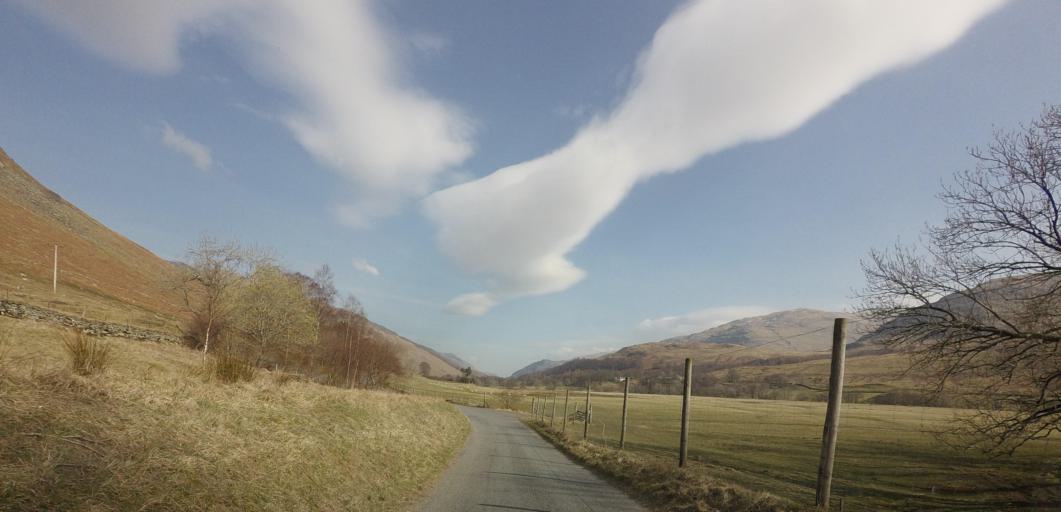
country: GB
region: Scotland
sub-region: Perth and Kinross
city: Comrie
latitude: 56.5985
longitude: -4.2762
